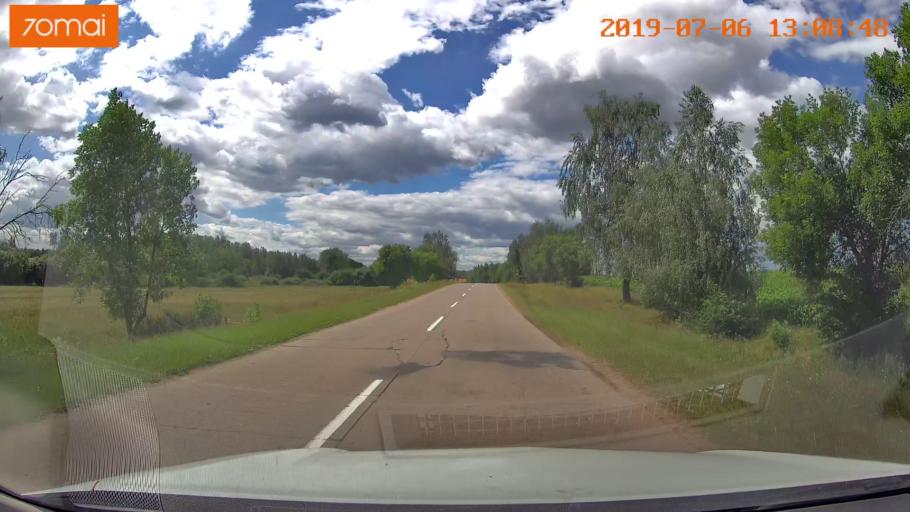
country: BY
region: Minsk
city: Enyerhyetykaw
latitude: 53.6664
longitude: 27.0182
